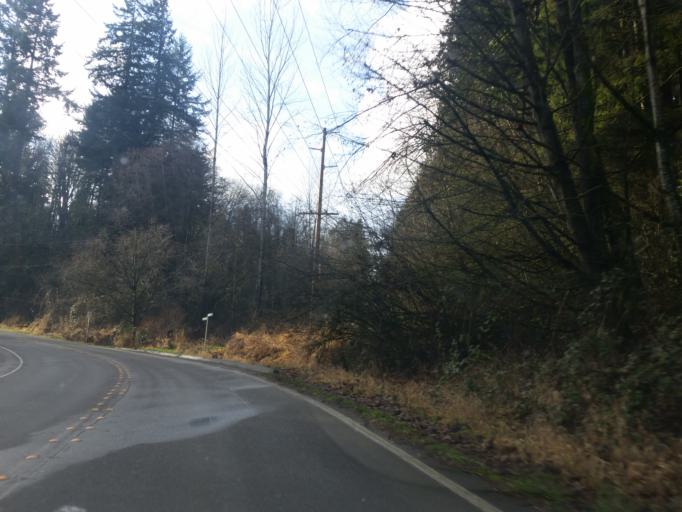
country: US
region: Washington
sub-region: King County
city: Woodinville
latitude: 47.7329
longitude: -122.1548
